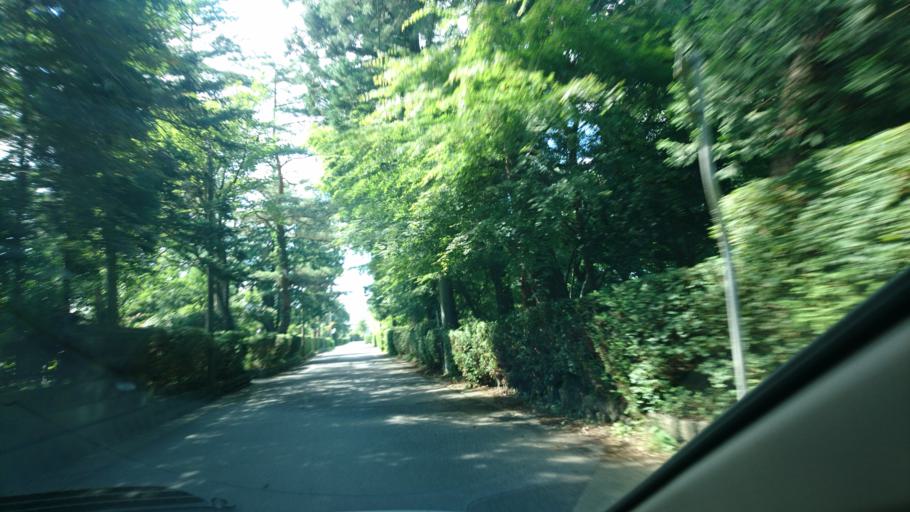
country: JP
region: Iwate
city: Mizusawa
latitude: 39.1946
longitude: 141.1224
